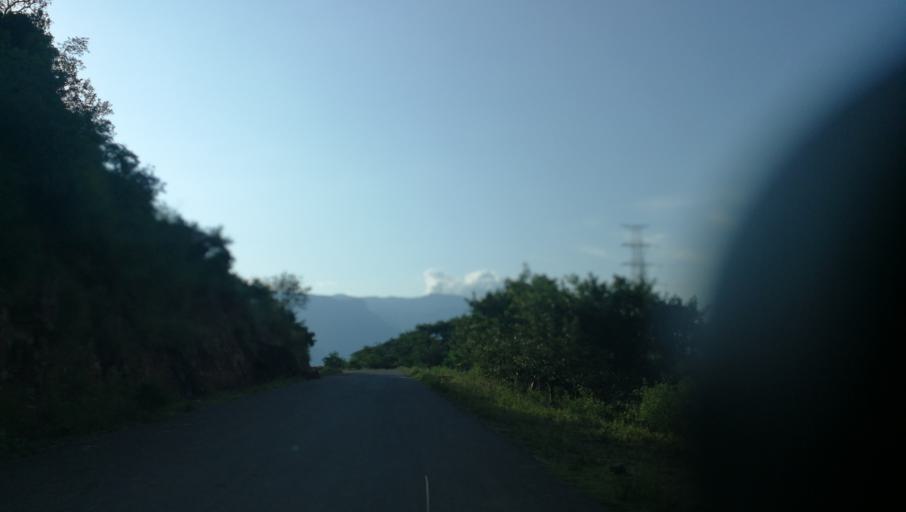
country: ET
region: Southern Nations, Nationalities, and People's Region
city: Areka
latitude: 6.8313
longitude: 37.3157
